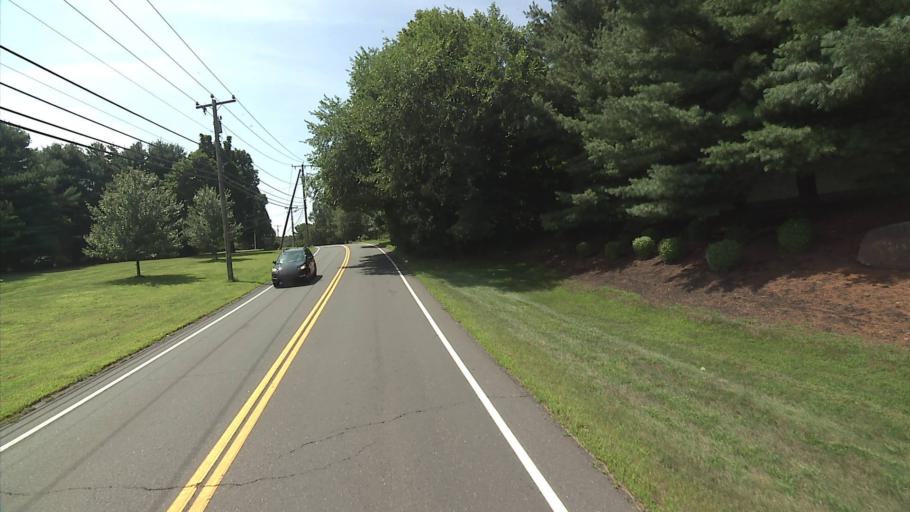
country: US
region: Connecticut
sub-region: Tolland County
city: Ellington
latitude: 41.8722
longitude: -72.4899
